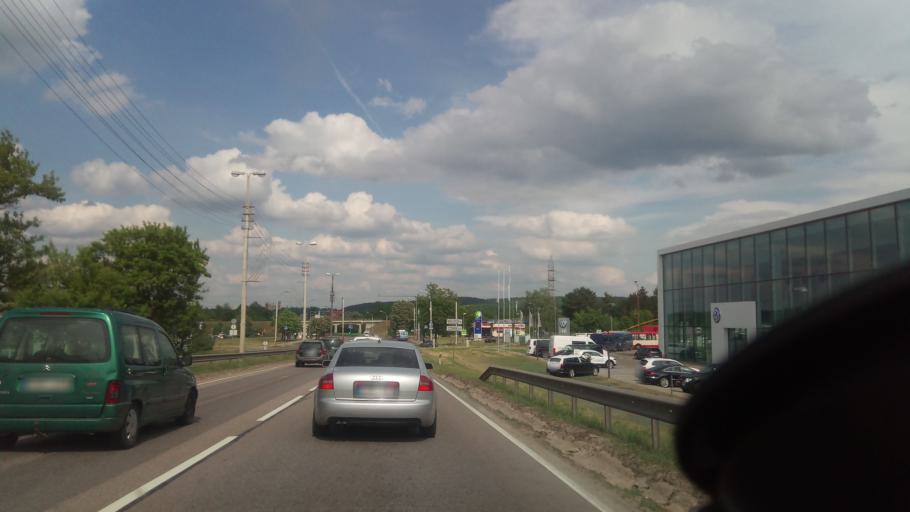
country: LT
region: Vilnius County
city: Lazdynai
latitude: 54.6443
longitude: 25.1994
